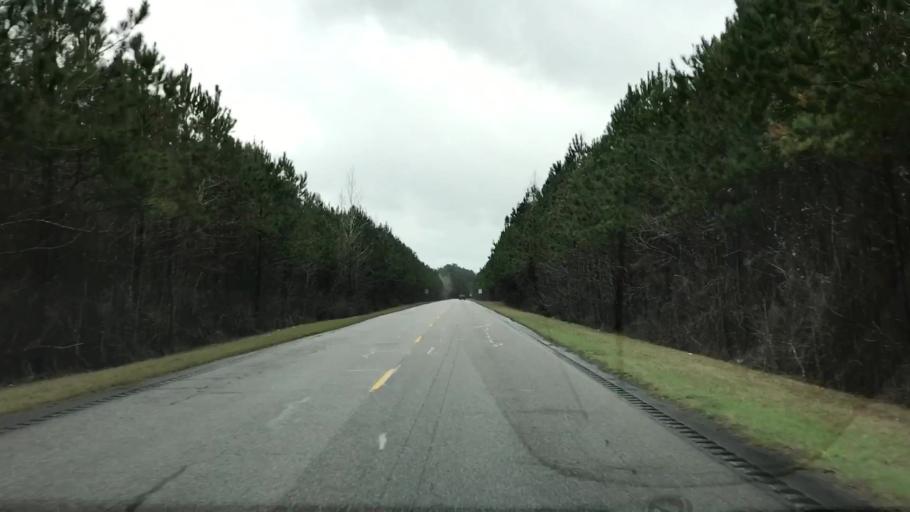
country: US
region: South Carolina
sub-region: Williamsburg County
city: Andrews
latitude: 33.5668
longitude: -79.4527
